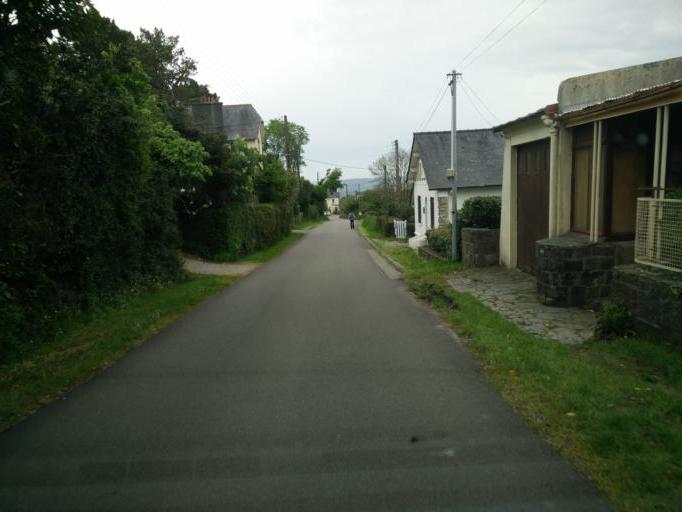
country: FR
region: Brittany
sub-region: Departement du Finistere
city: Logonna-Daoulas
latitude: 48.2917
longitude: -4.2763
